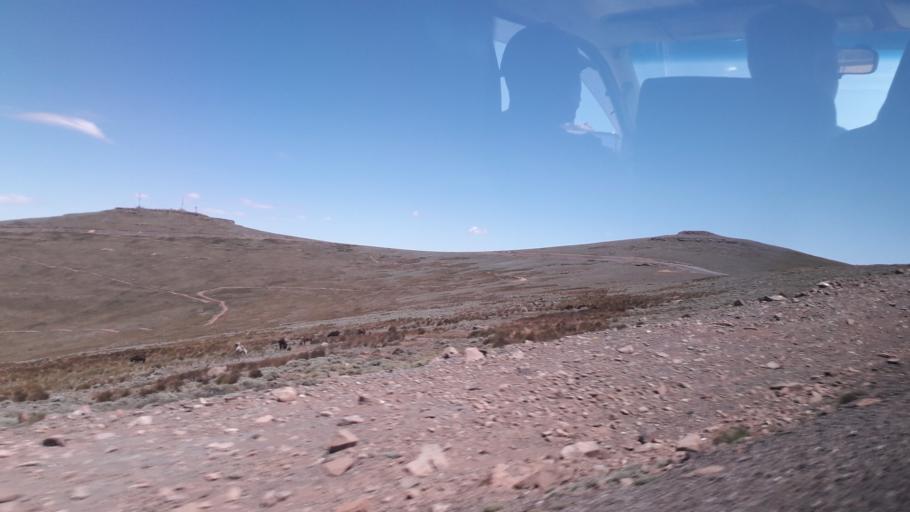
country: ZA
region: Orange Free State
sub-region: Thabo Mofutsanyana District Municipality
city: Phuthaditjhaba
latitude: -28.8160
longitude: 28.7360
